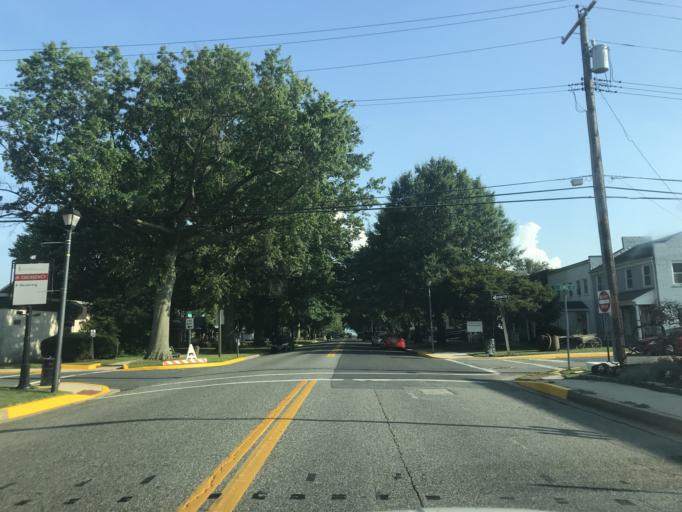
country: US
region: Maryland
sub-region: Harford County
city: Havre de Grace
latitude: 39.5427
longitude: -76.0915
